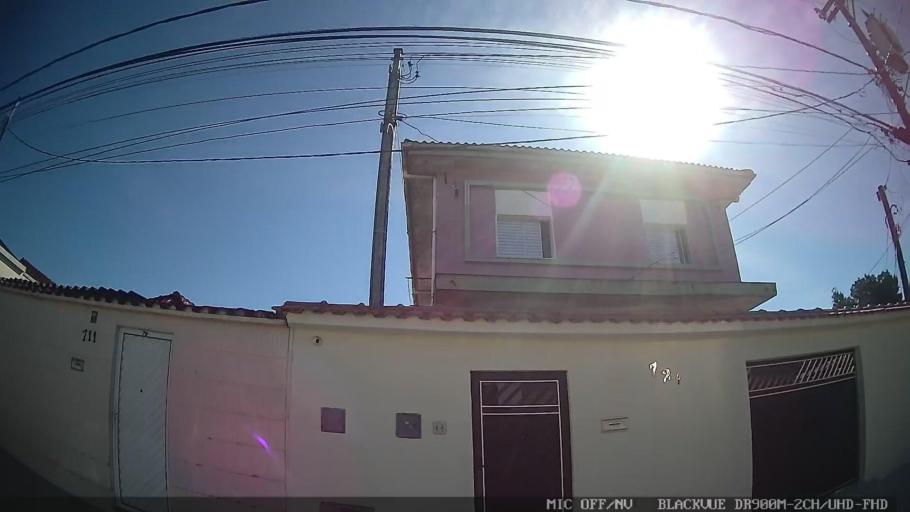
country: BR
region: Sao Paulo
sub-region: Santos
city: Santos
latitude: -23.9427
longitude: -46.2918
